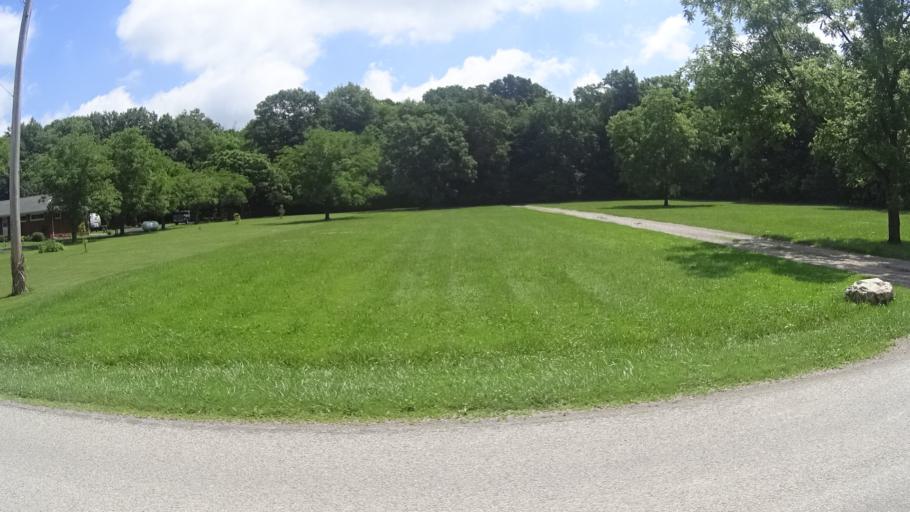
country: US
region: Ohio
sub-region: Huron County
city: Wakeman
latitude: 41.2848
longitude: -82.3625
